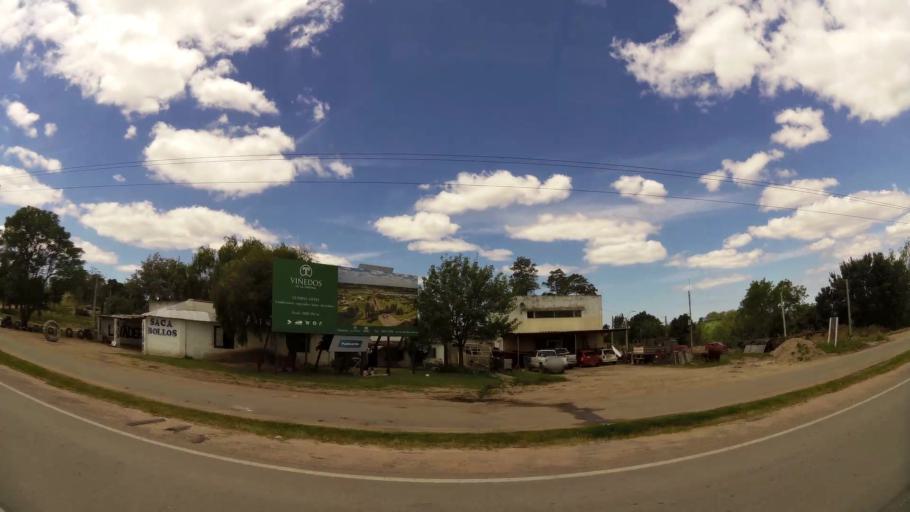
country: UY
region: Canelones
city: Colonia Nicolich
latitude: -34.8246
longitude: -55.9959
